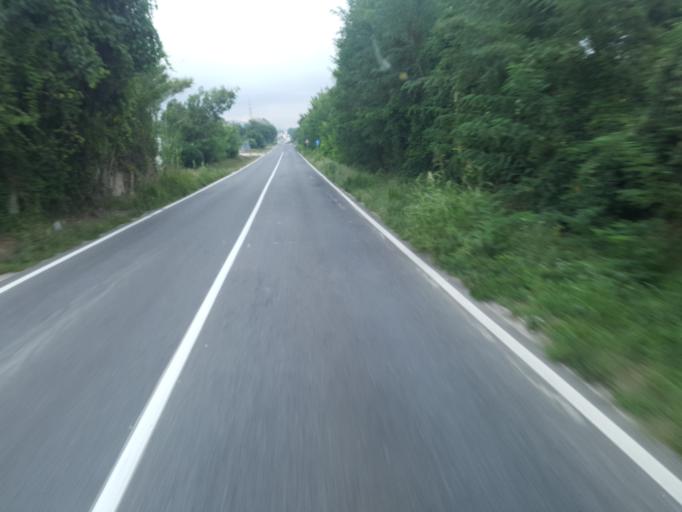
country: IT
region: Campania
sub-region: Provincia di Caserta
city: Pignataro Maggiore
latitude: 41.1683
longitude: 14.1505
